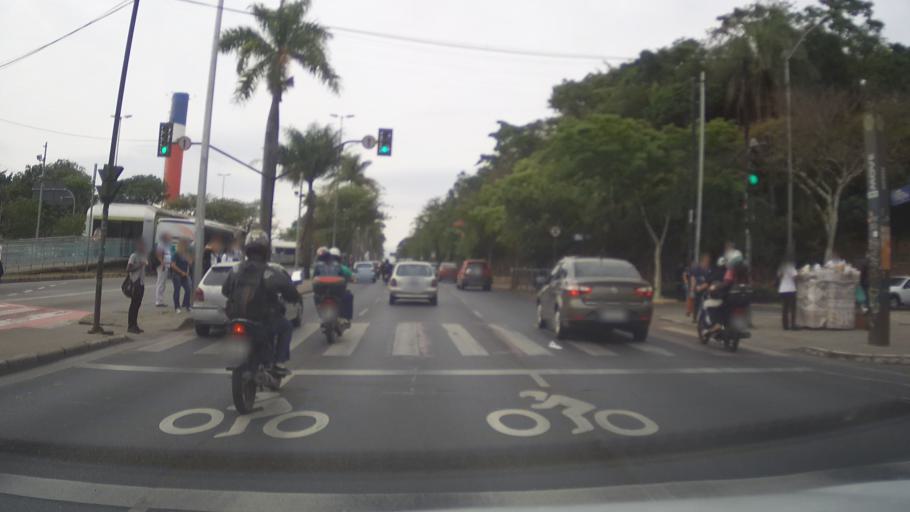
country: BR
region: Minas Gerais
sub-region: Belo Horizonte
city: Belo Horizonte
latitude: -19.8629
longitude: -43.9582
